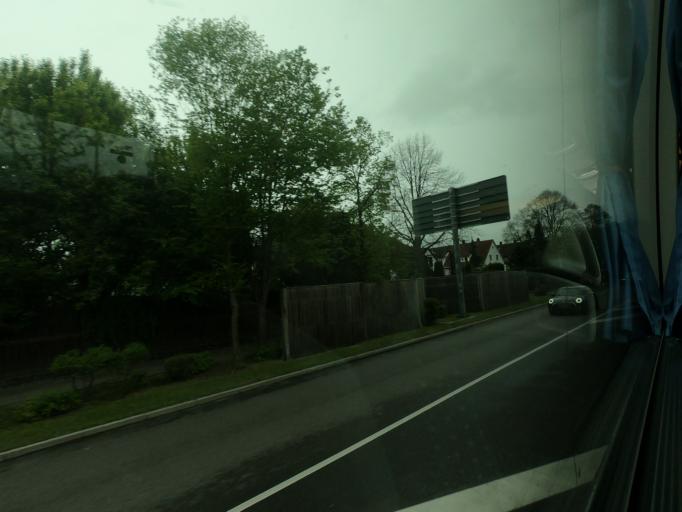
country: DE
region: Baden-Wuerttemberg
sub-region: Regierungsbezirk Stuttgart
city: Heidenheim an der Brenz
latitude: 48.7055
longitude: 10.1632
